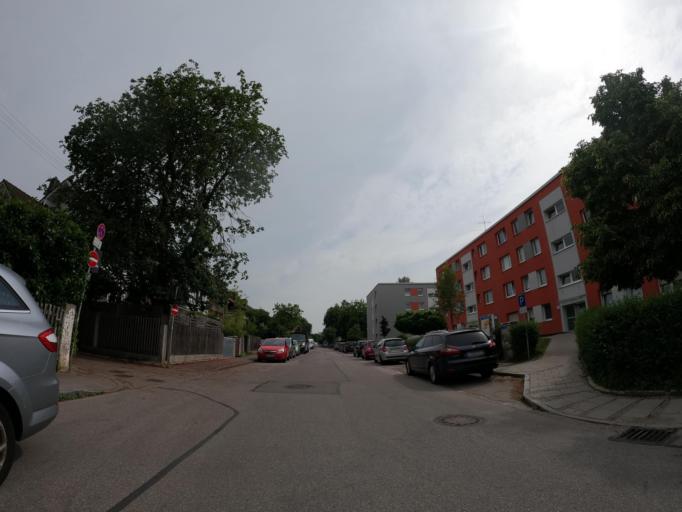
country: DE
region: Bavaria
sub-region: Upper Bavaria
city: Unterhaching
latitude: 48.0696
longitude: 11.6051
